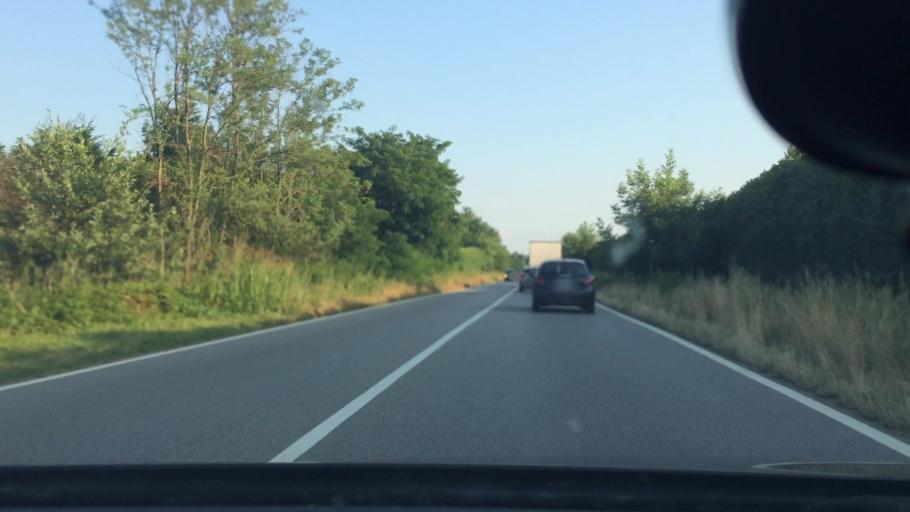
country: IT
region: Lombardy
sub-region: Citta metropolitana di Milano
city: Mantegazza
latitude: 45.5185
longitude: 8.9605
